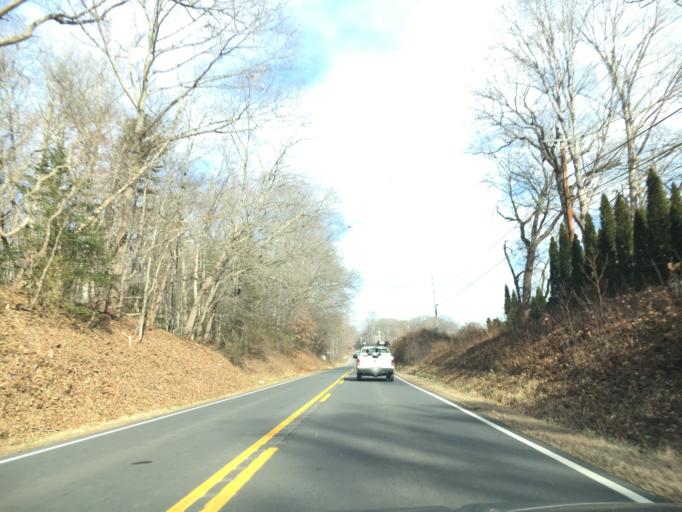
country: US
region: Virginia
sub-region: Culpeper County
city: Culpeper
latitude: 38.6255
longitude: -77.9397
